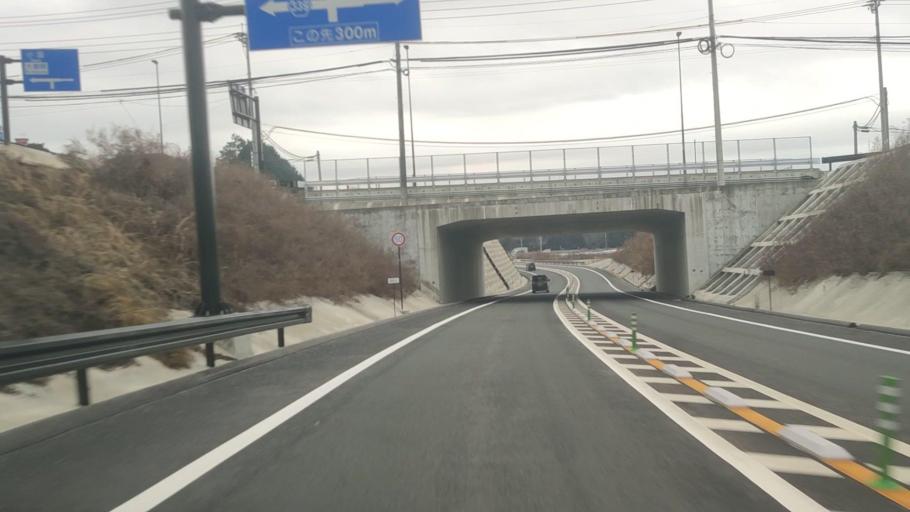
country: JP
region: Kumamoto
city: Ozu
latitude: 32.8906
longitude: 130.8964
